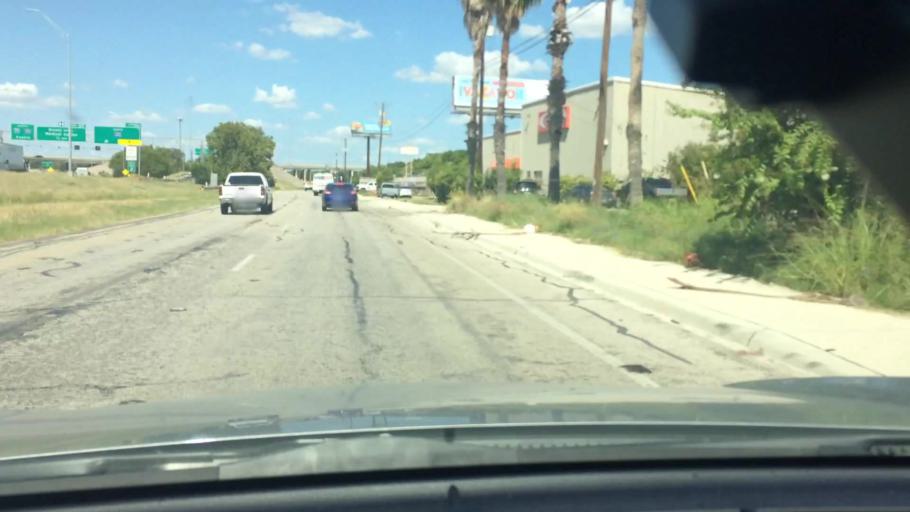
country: US
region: Texas
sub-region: Bexar County
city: Kirby
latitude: 29.4525
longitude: -98.4168
